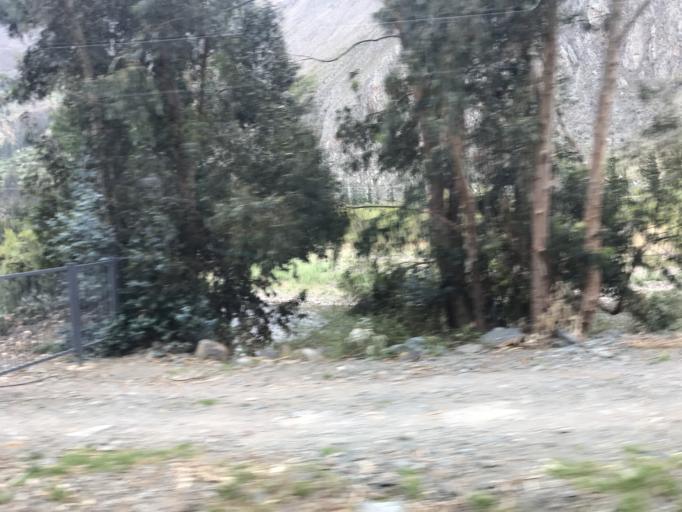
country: PE
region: Cusco
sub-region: Provincia de Urubamba
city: Ollantaytambo
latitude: -13.2423
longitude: -72.2942
